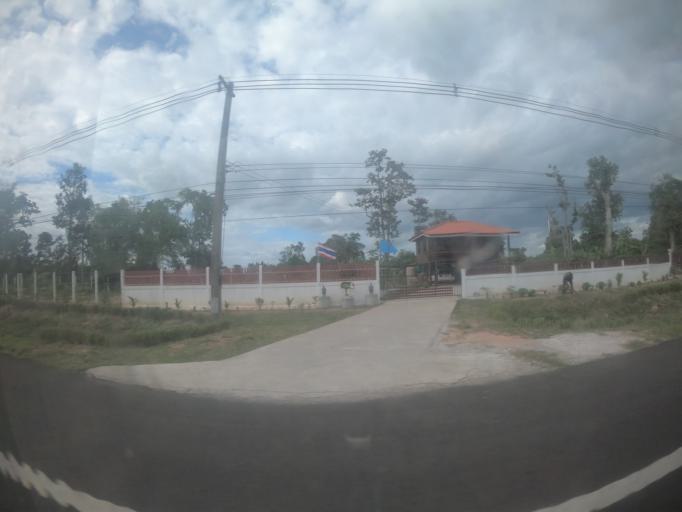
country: TH
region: Surin
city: Prasat
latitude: 14.5701
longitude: 103.4886
